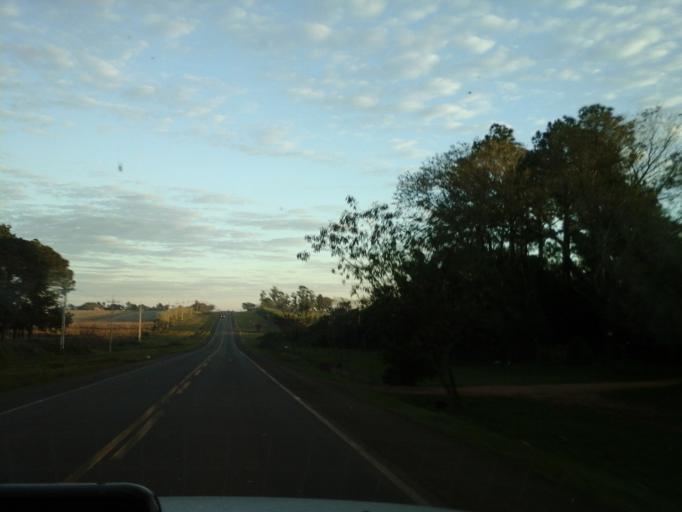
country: PY
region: Misiones
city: San Patricio
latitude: -27.0217
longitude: -56.7118
